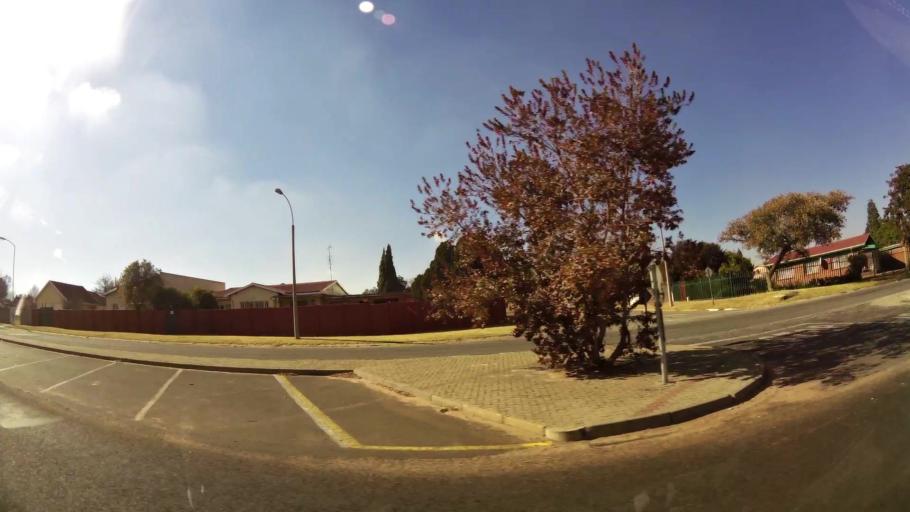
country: ZA
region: Gauteng
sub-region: City of Johannesburg Metropolitan Municipality
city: Roodepoort
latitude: -26.1494
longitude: 27.8226
